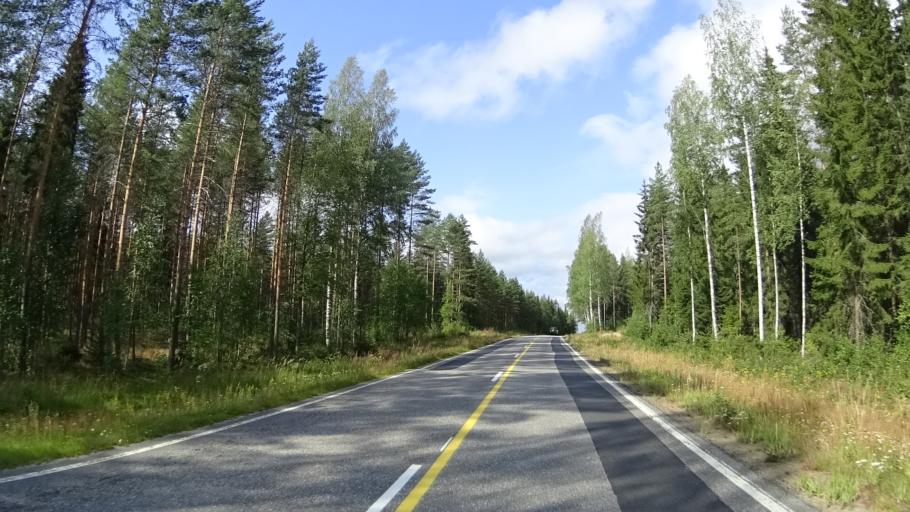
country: FI
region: Pirkanmaa
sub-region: Tampere
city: Luopioinen
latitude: 61.4813
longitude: 24.7455
